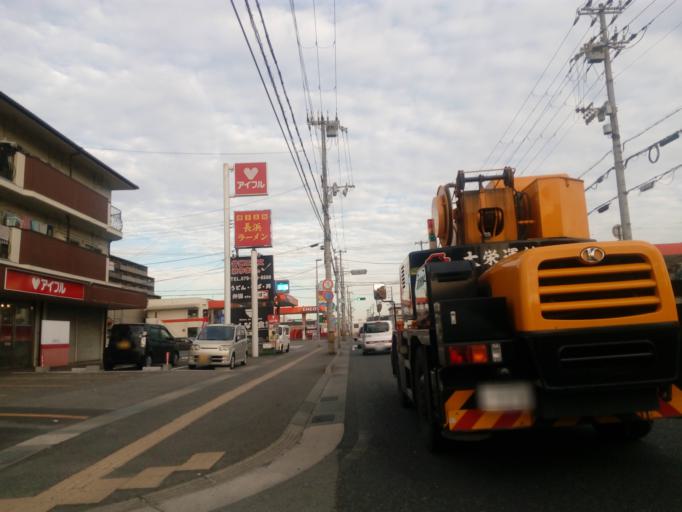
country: JP
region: Hyogo
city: Himeji
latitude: 34.7954
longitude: 134.6321
